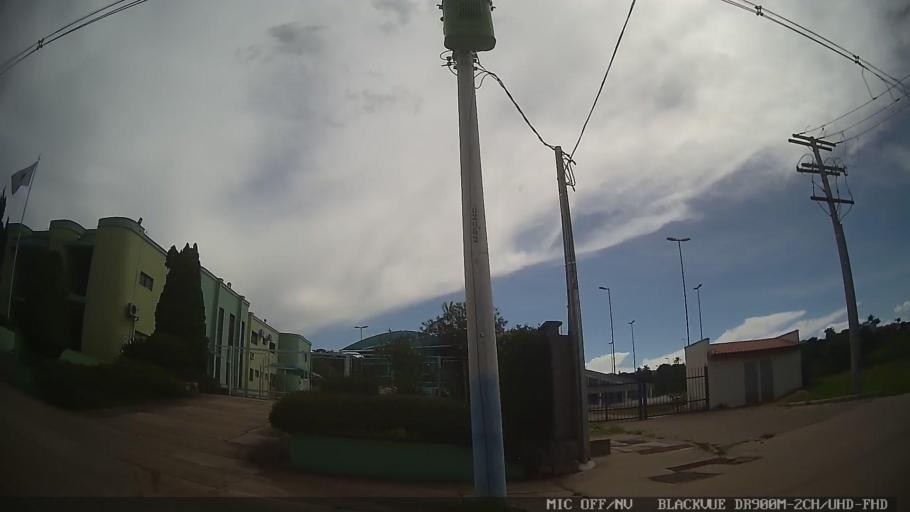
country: BR
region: Sao Paulo
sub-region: Conchas
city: Conchas
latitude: -23.0195
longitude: -48.0001
